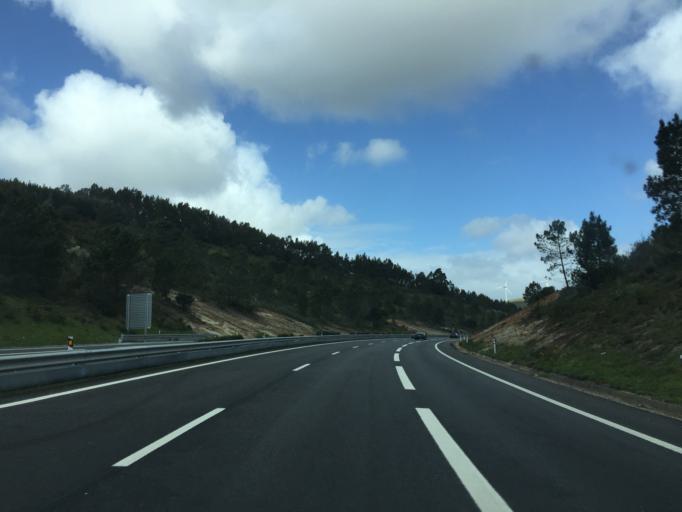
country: PT
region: Lisbon
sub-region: Sobral de Monte Agraco
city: Sobral de Monte Agraco
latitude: 39.0177
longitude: -9.2167
